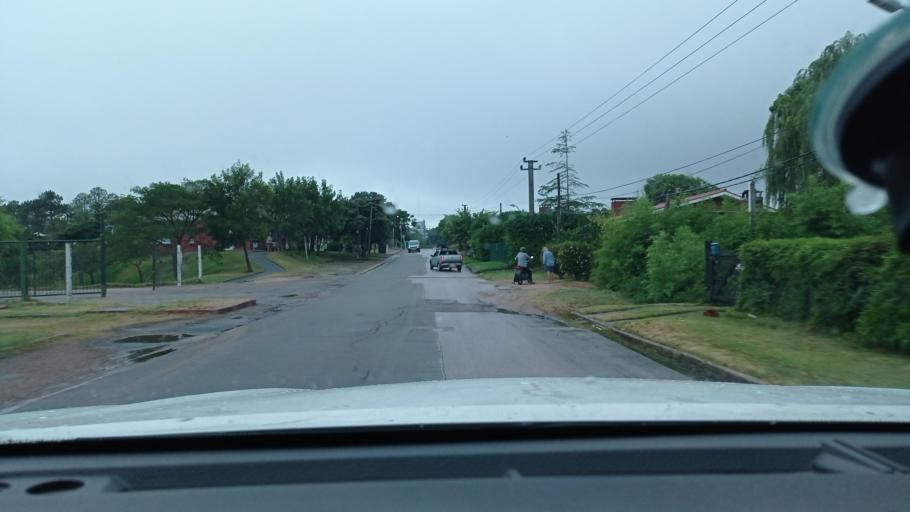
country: UY
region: Maldonado
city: Maldonado
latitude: -34.9148
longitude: -54.9646
